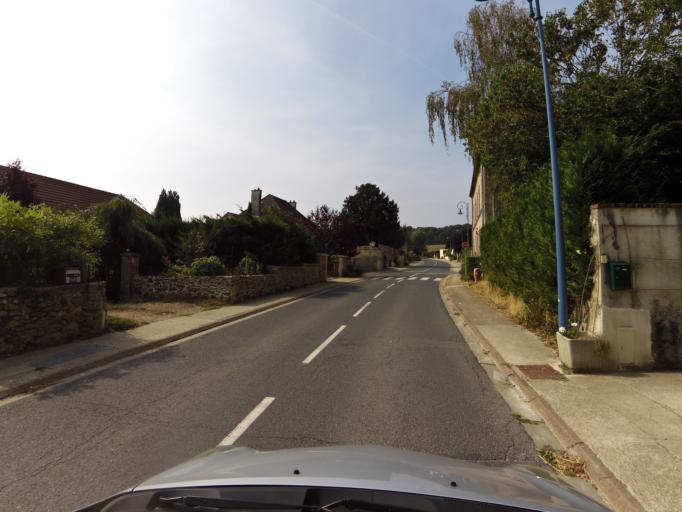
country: FR
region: Champagne-Ardenne
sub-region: Departement de la Marne
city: Damery
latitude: 49.1297
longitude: 3.9182
